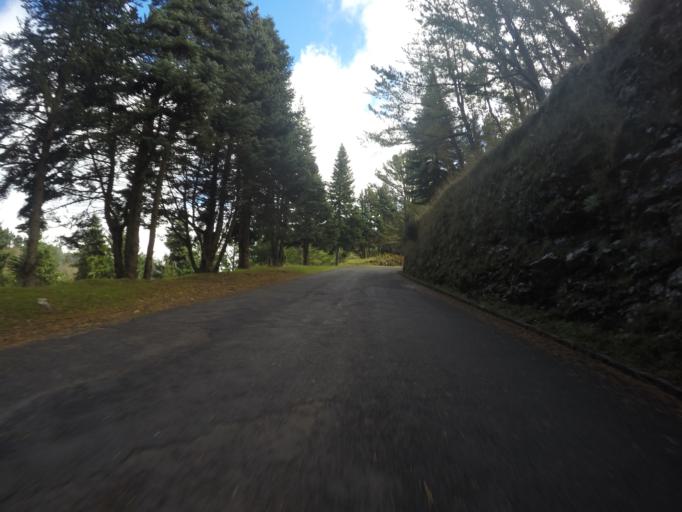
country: PT
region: Madeira
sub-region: Funchal
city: Nossa Senhora do Monte
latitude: 32.6967
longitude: -16.8807
